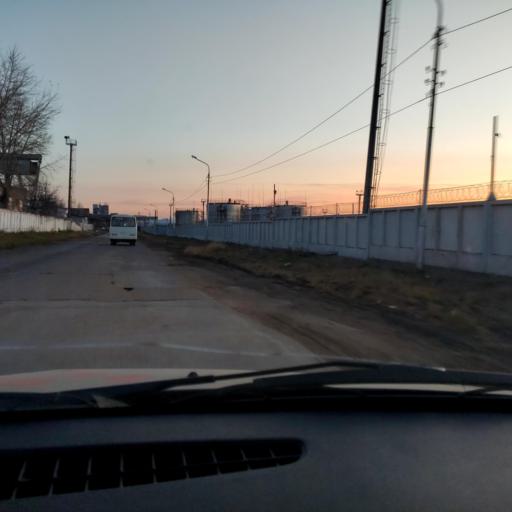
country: RU
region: Bashkortostan
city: Ufa
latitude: 54.8489
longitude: 56.0822
